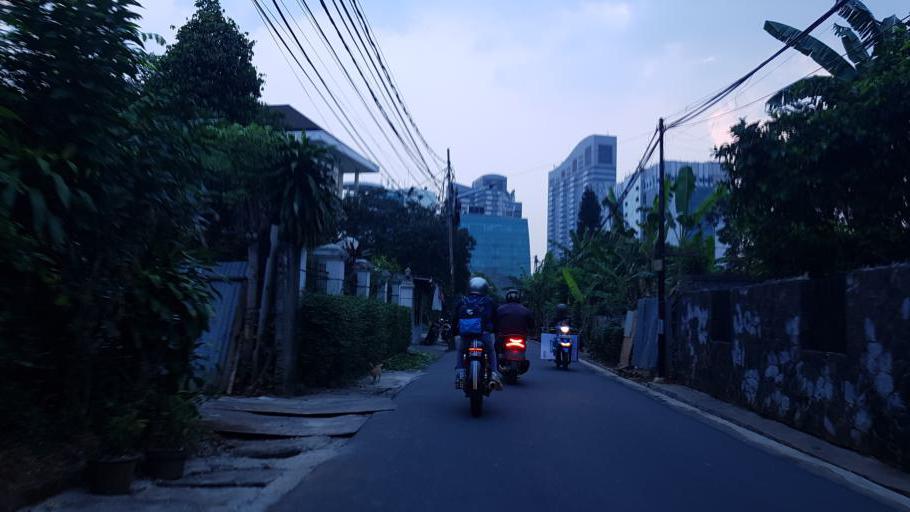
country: ID
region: West Java
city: Pamulang
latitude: -6.2981
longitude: 106.7884
